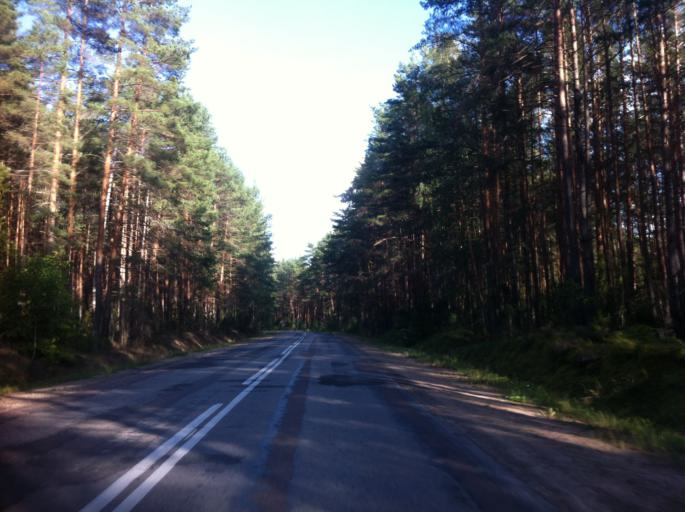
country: RU
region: Pskov
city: Izborsk
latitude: 57.8026
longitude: 27.7755
